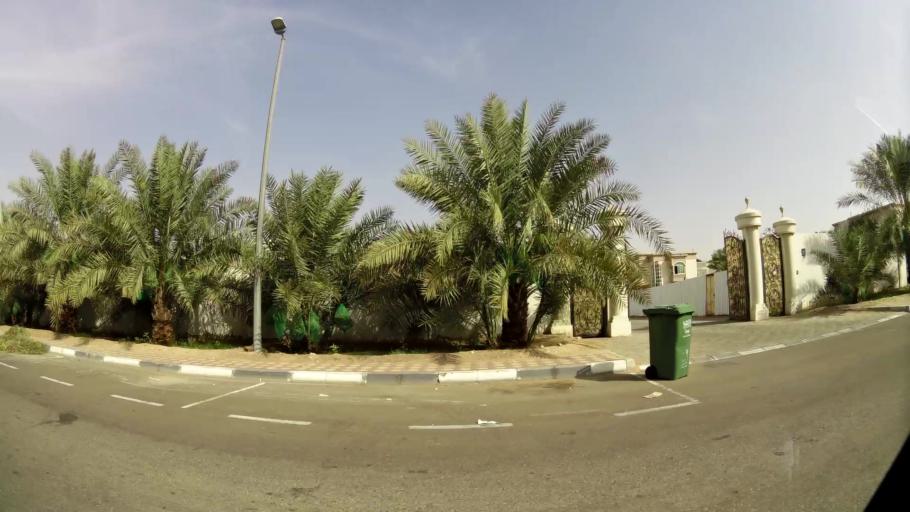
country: AE
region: Abu Dhabi
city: Al Ain
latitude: 24.1444
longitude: 55.6980
